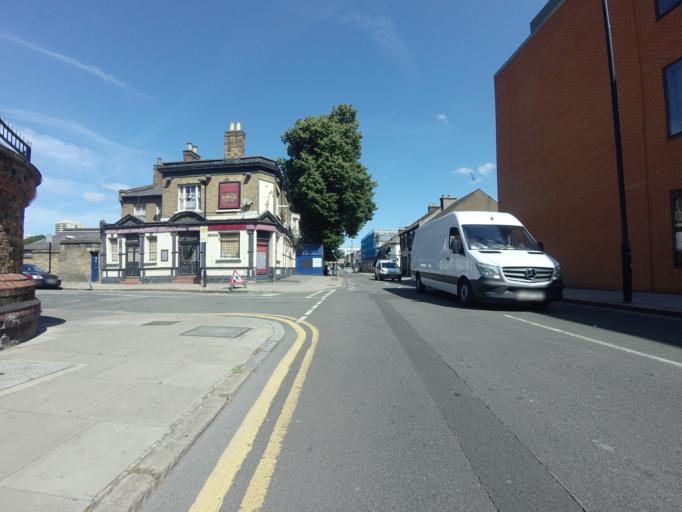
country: GB
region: England
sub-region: Greater London
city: Poplar
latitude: 51.5445
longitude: 0.0083
